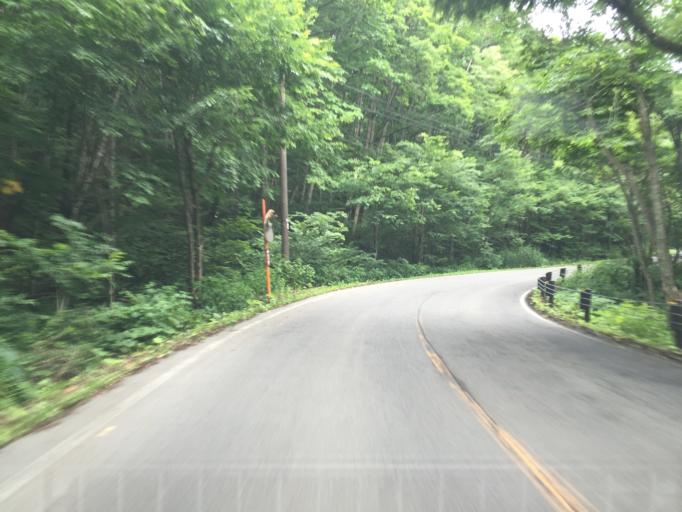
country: JP
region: Fukushima
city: Inawashiro
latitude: 37.7149
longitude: 140.0622
